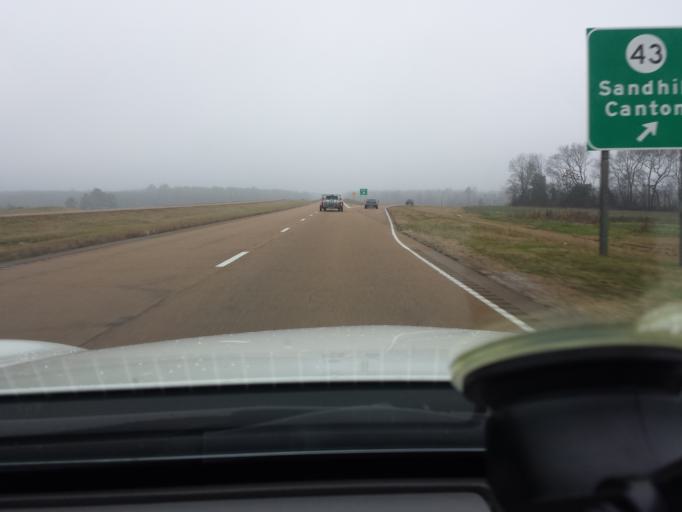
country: US
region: Mississippi
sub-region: Madison County
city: Canton
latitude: 32.4988
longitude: -89.8790
